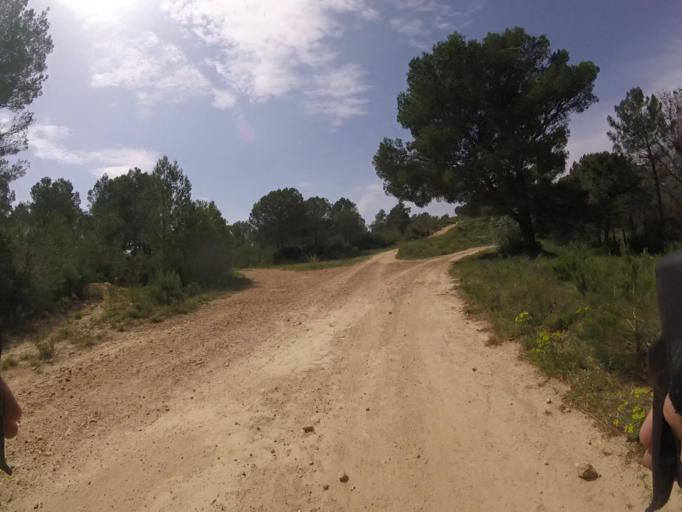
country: ES
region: Valencia
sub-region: Provincia de Castello
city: Cuevas de Vinroma
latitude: 40.2787
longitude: 0.1228
